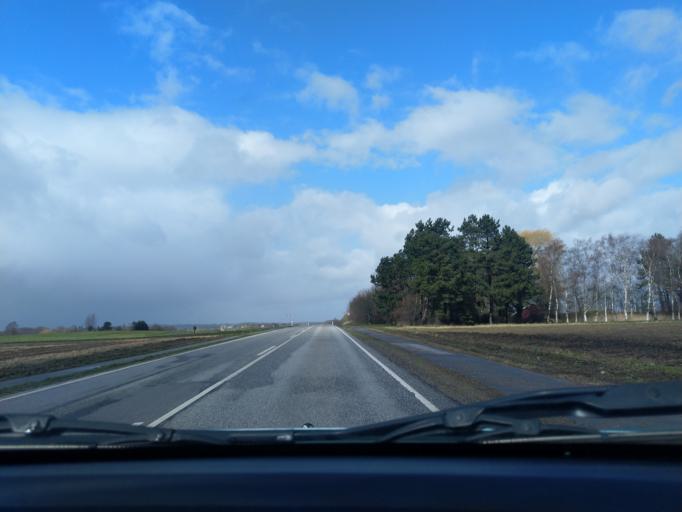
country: DK
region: Zealand
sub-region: Naestved Kommune
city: Naestved
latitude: 55.3097
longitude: 11.6860
